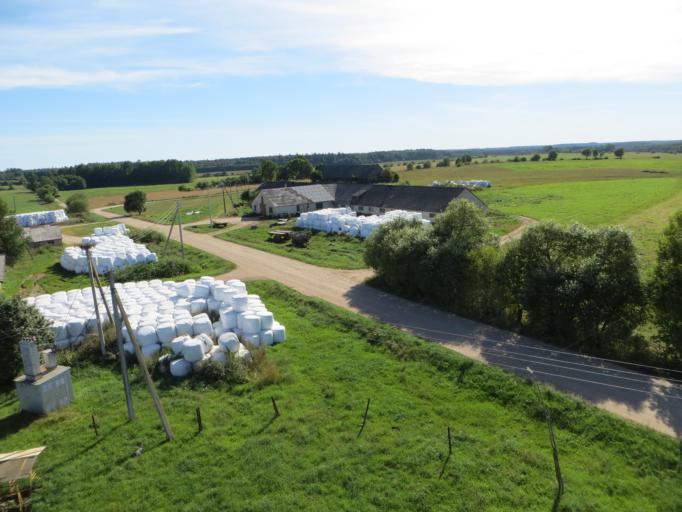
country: LT
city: Obeliai
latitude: 55.7305
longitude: 25.3588
